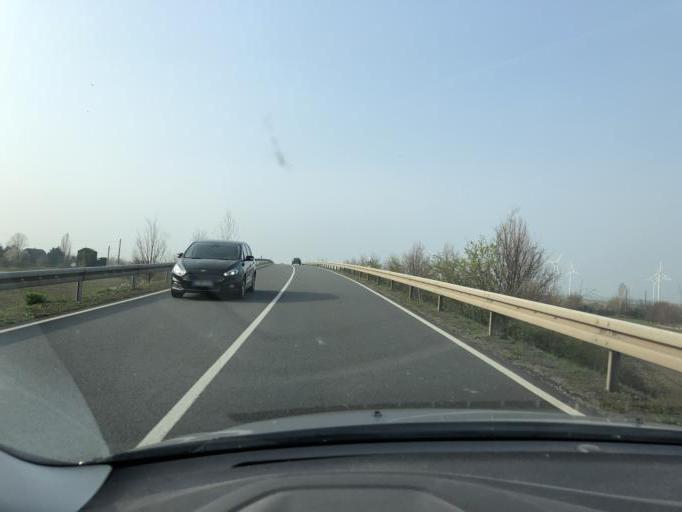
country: DE
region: Saxony-Anhalt
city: Brehna
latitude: 51.5557
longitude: 12.2302
